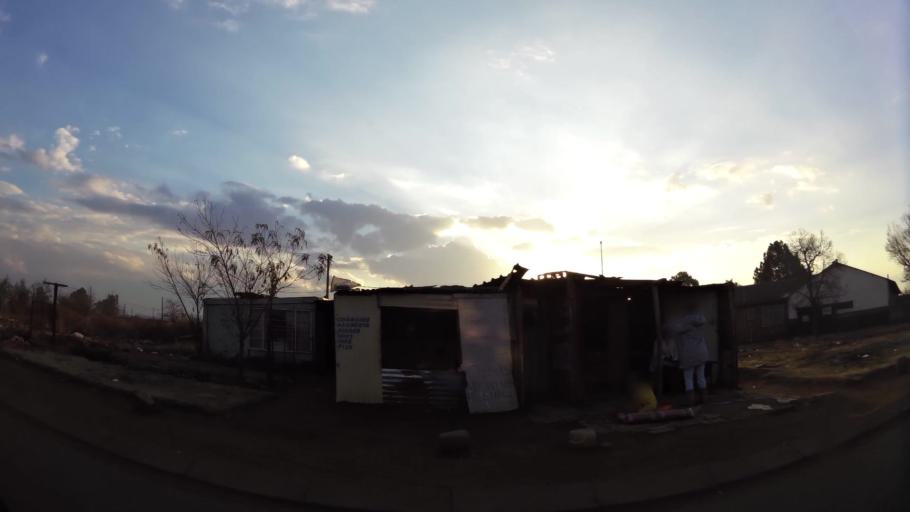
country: ZA
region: Gauteng
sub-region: City of Johannesburg Metropolitan Municipality
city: Orange Farm
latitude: -26.5346
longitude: 27.8513
